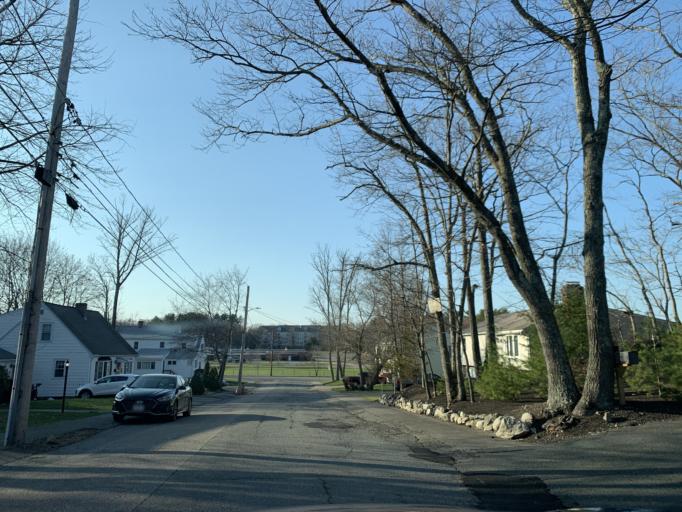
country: US
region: Massachusetts
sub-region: Norfolk County
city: Norwood
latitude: 42.2019
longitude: -71.2024
